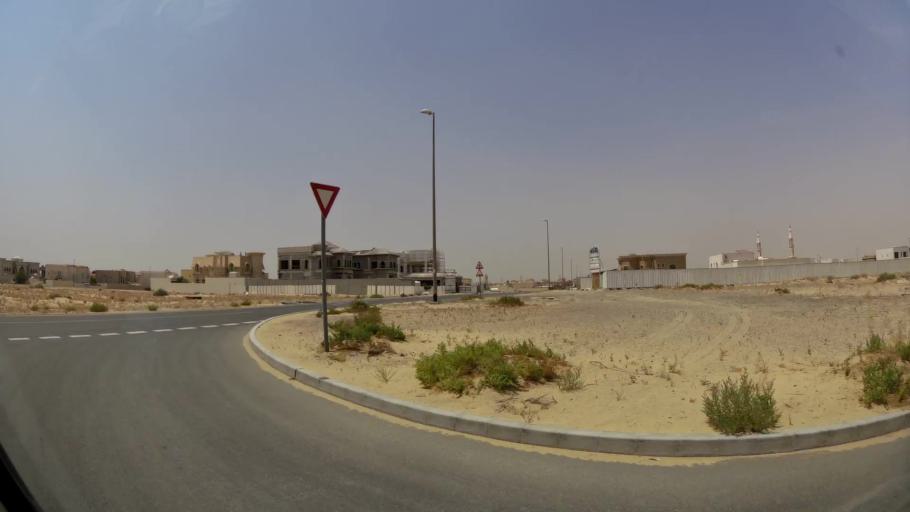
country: AE
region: Ash Shariqah
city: Sharjah
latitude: 25.2419
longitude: 55.5007
